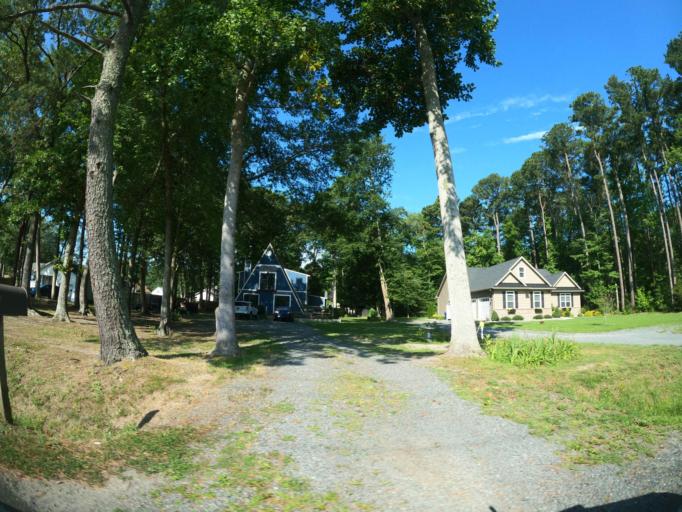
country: US
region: Delaware
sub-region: Sussex County
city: Ocean View
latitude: 38.4764
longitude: -75.1164
